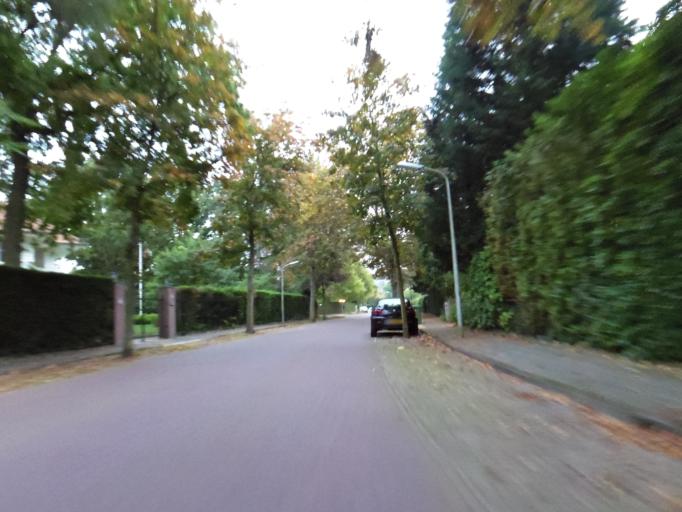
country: NL
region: South Holland
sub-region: Gemeente Wassenaar
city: Wassenaar
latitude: 52.1254
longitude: 4.3626
